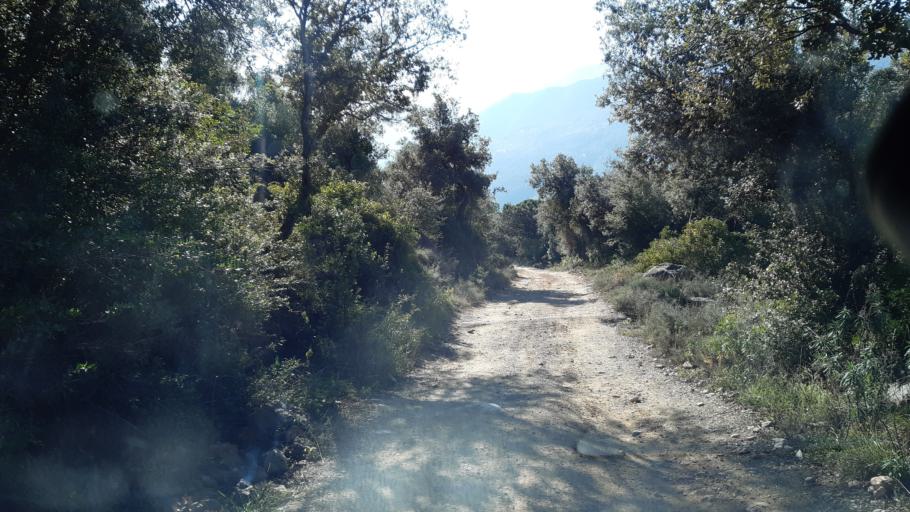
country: ES
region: Catalonia
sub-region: Provincia de Girona
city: la Cellera de Ter
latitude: 42.0210
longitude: 2.6083
